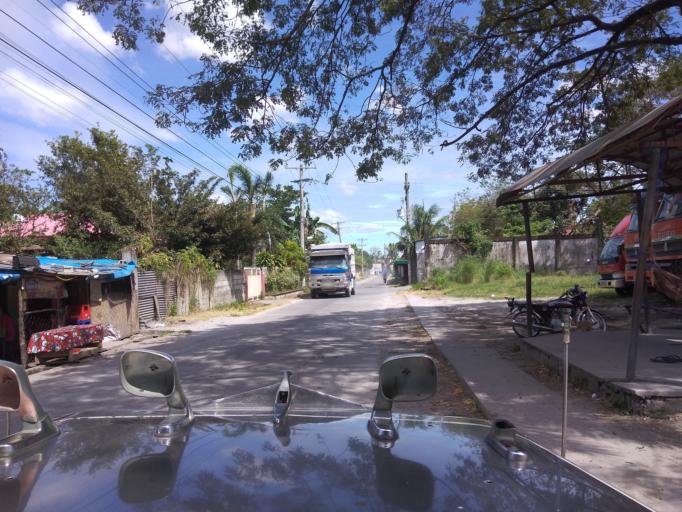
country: PH
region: Central Luzon
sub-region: Province of Pampanga
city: Magliman
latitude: 15.0370
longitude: 120.6528
